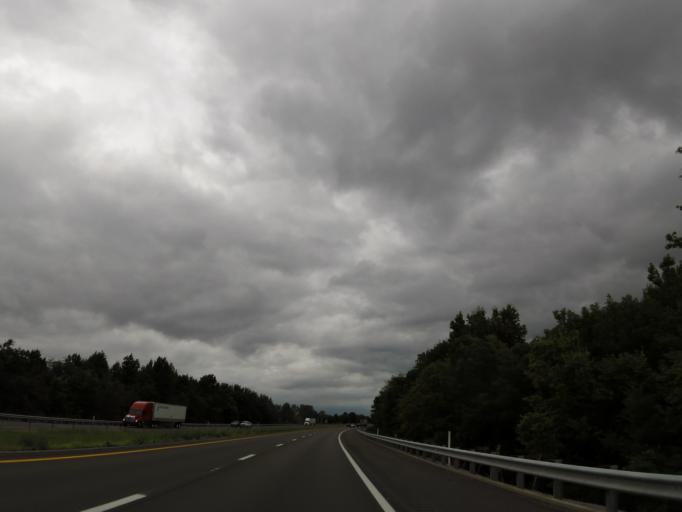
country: US
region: Illinois
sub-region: Massac County
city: Metropolis
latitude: 37.1115
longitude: -88.6929
